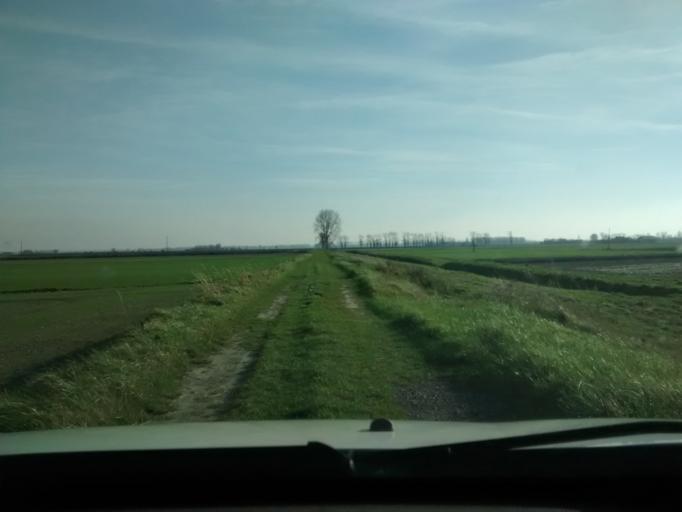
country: FR
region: Brittany
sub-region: Departement d'Ille-et-Vilaine
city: Roz-sur-Couesnon
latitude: 48.6104
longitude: -1.5874
